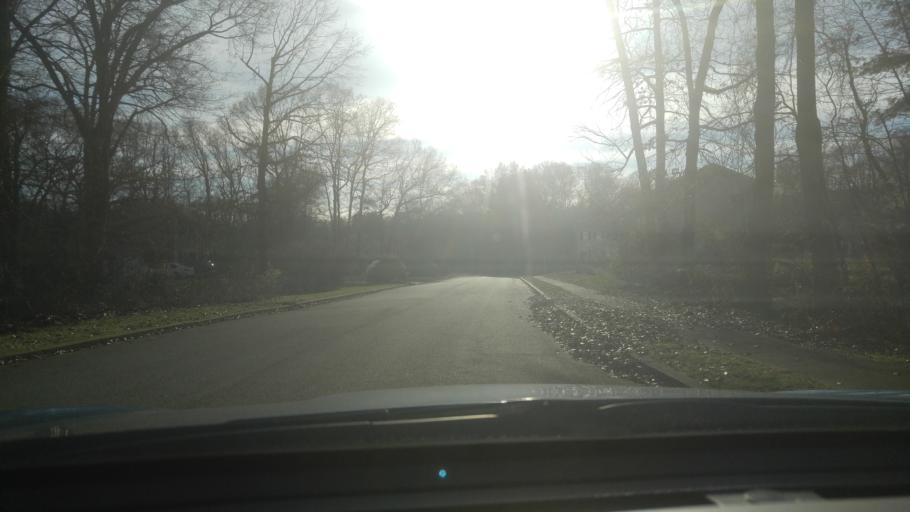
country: US
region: Rhode Island
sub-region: Kent County
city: East Greenwich
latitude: 41.6832
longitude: -71.4717
